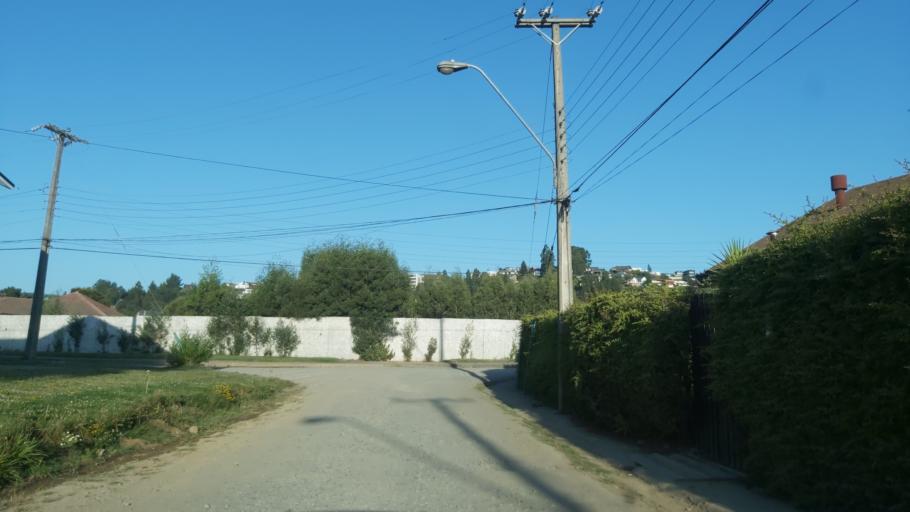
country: CL
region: Biobio
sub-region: Provincia de Concepcion
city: Tome
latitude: -36.5313
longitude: -72.9314
